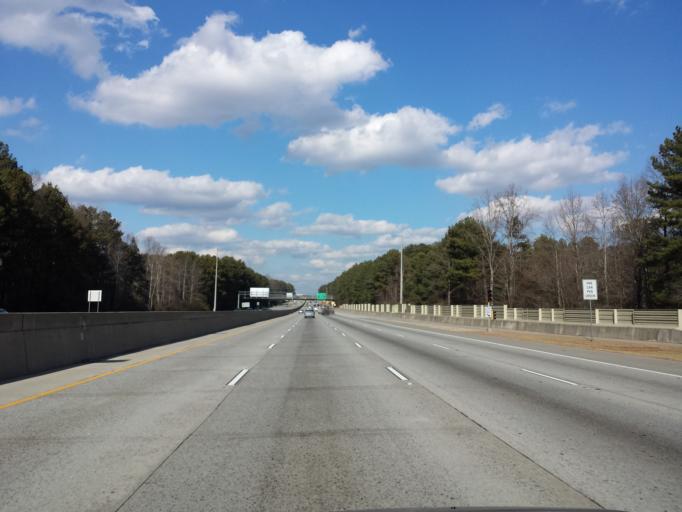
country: US
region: Georgia
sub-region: Fulton County
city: Alpharetta
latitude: 34.0703
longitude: -84.2710
